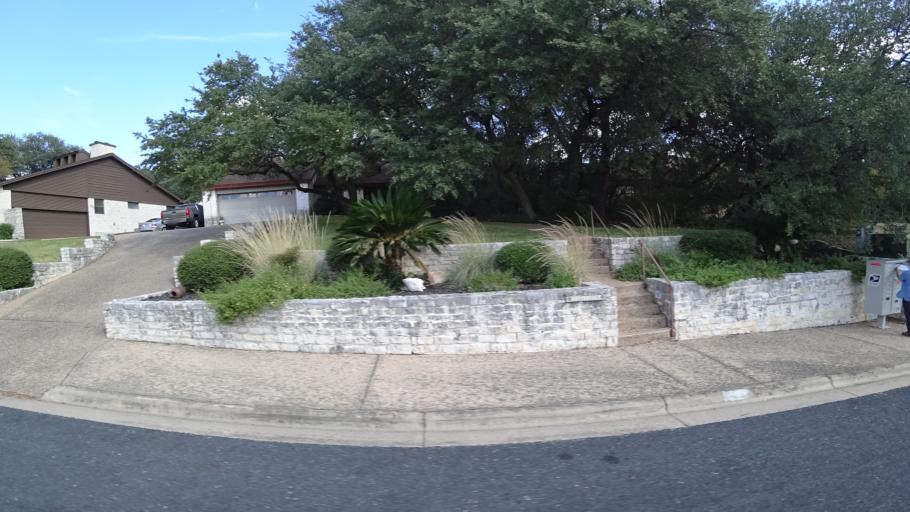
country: US
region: Texas
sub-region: Williamson County
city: Anderson Mill
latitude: 30.4241
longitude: -97.8017
